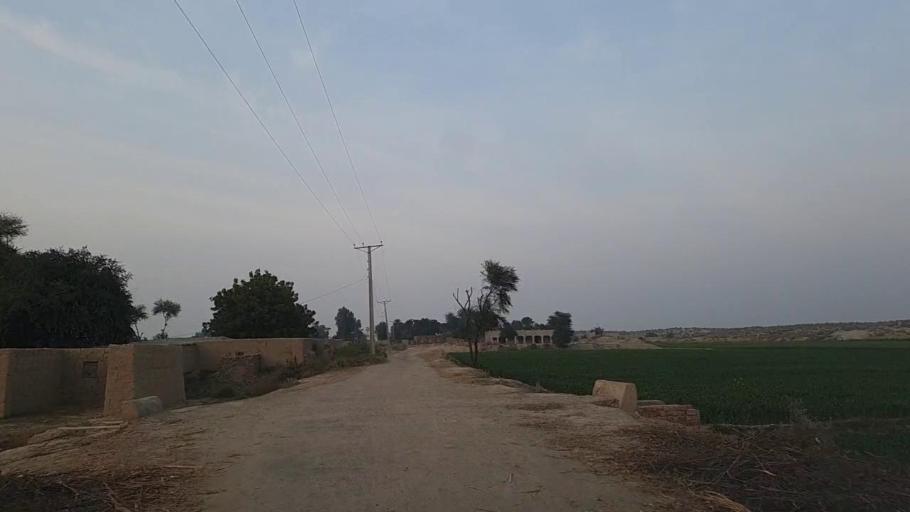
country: PK
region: Sindh
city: Jam Sahib
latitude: 26.4739
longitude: 68.5482
